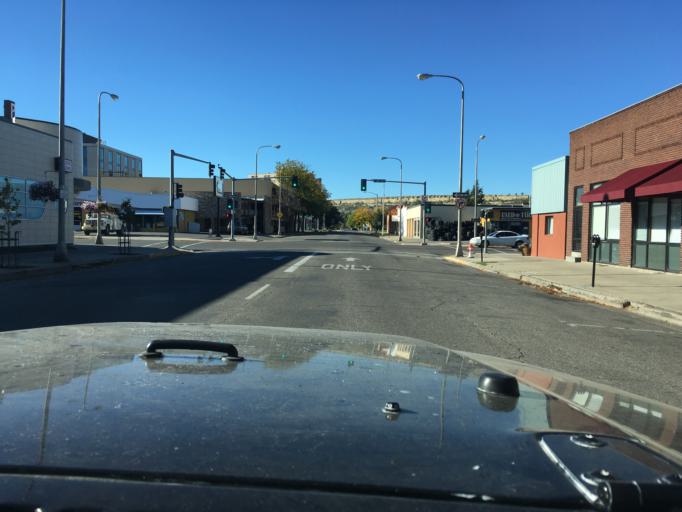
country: US
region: Montana
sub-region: Yellowstone County
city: Billings
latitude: 45.7835
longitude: -108.5017
